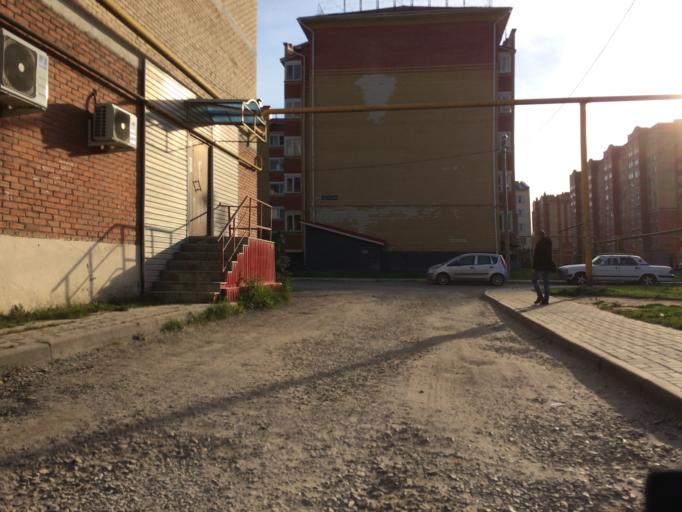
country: RU
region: Mariy-El
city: Yoshkar-Ola
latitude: 56.6303
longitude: 47.8519
